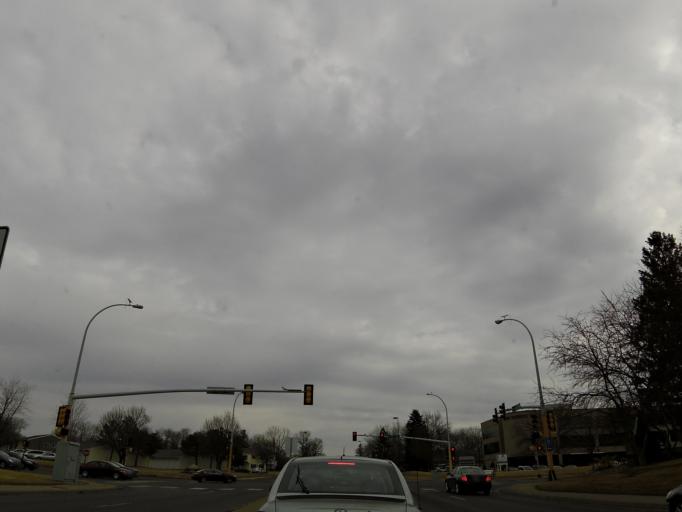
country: US
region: Minnesota
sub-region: Hennepin County
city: Bloomington
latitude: 44.8655
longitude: -93.3219
